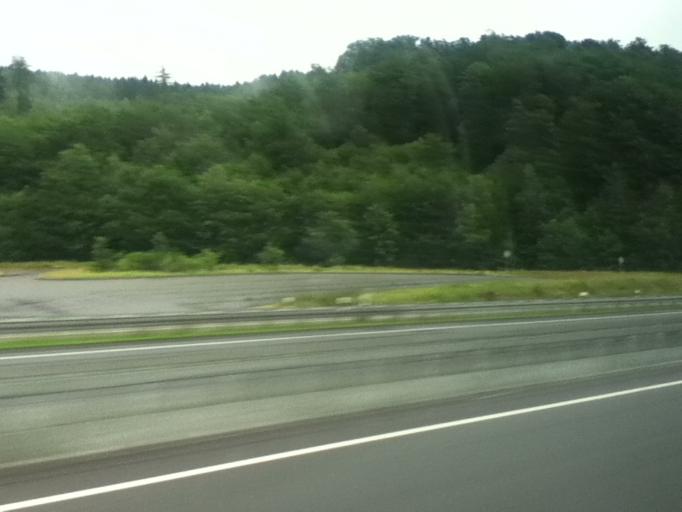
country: DE
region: Hesse
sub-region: Regierungsbezirk Kassel
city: Herleshausen
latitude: 51.0072
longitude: 10.1820
